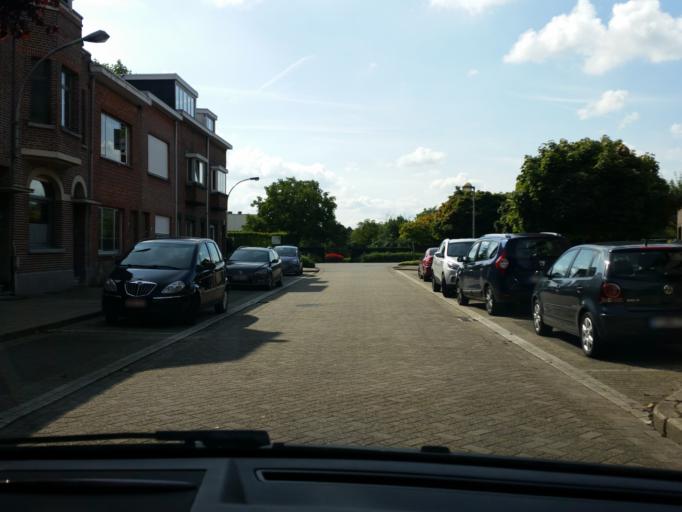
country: BE
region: Flanders
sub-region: Provincie Antwerpen
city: Edegem
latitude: 51.1542
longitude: 4.4393
